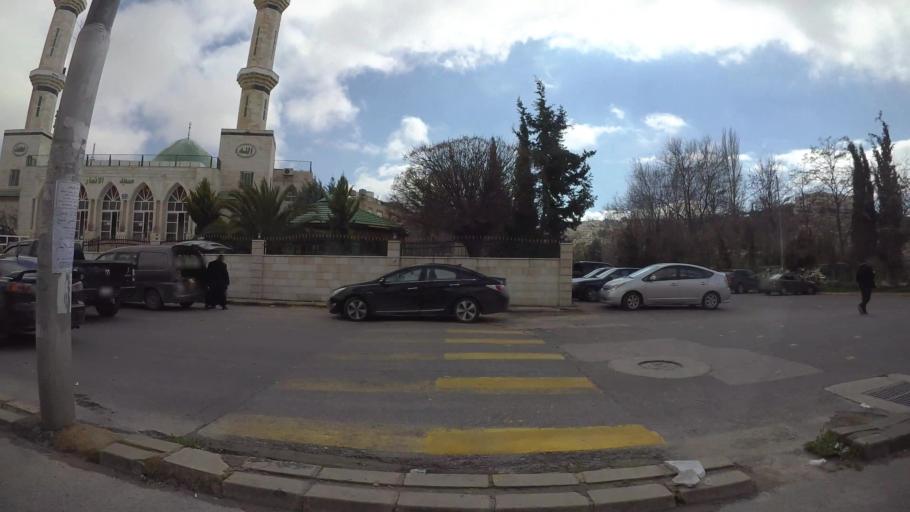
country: JO
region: Amman
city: Al Jubayhah
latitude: 32.0625
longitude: 35.8836
